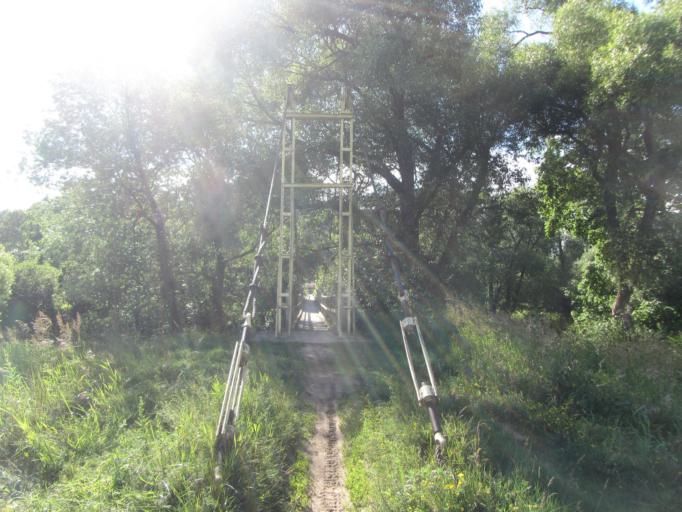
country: LT
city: Ramygala
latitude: 55.6308
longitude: 24.1168
